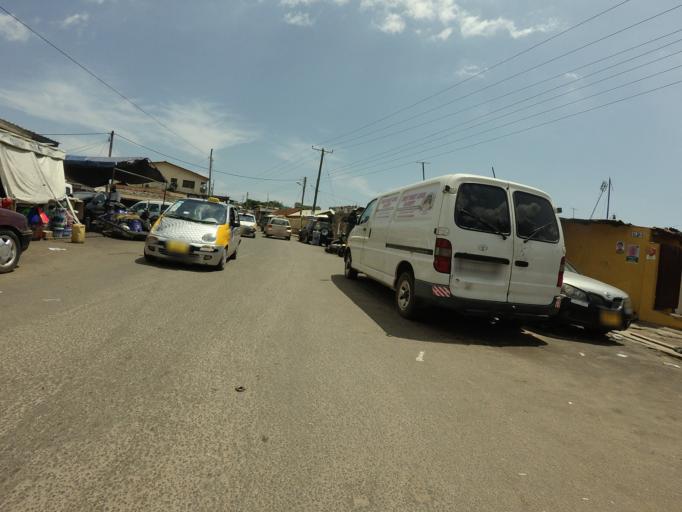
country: GH
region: Greater Accra
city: Accra
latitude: 5.5802
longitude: -0.2036
